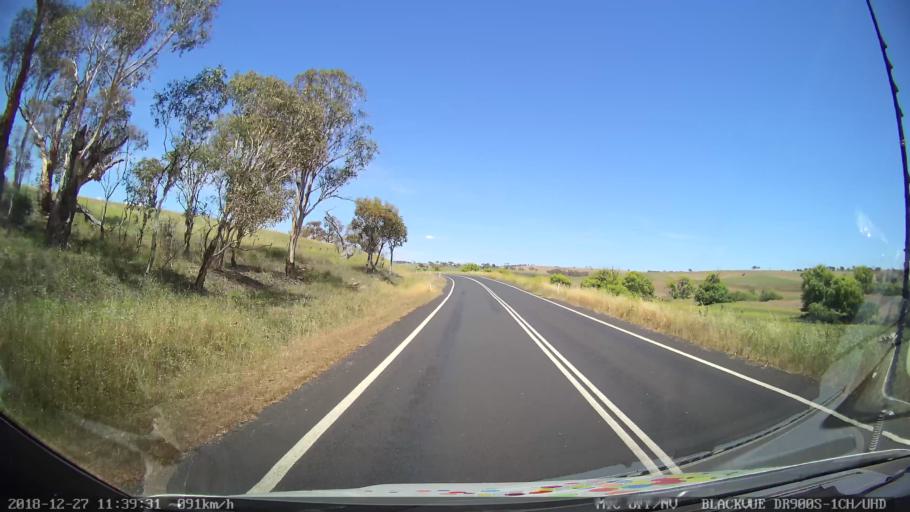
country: AU
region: New South Wales
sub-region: Bathurst Regional
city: Perthville
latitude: -33.5145
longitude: 149.4989
